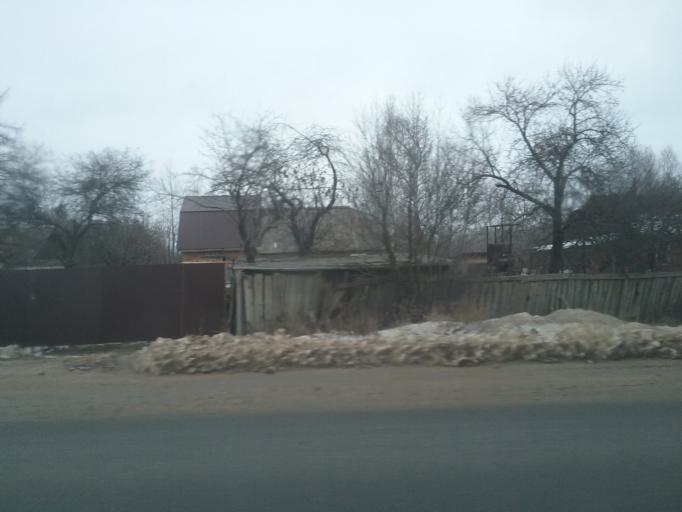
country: RU
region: Tula
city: Bolokhovo
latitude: 54.0549
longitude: 37.8085
